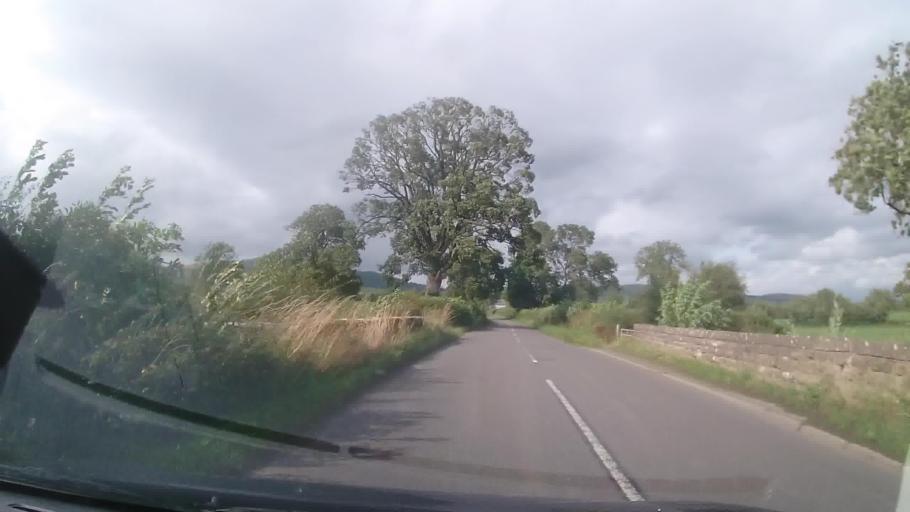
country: GB
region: England
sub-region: Shropshire
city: Lydham
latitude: 52.5119
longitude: -2.9651
